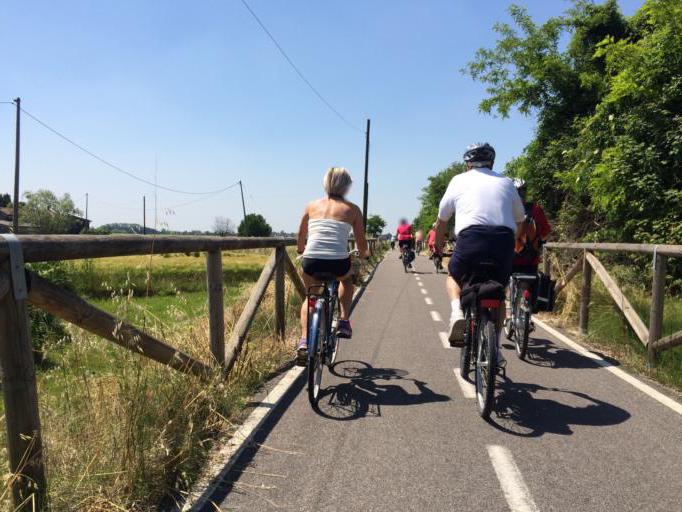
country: IT
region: Veneto
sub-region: Provincia di Vicenza
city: Ponte di Barbarano
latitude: 45.4071
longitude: 11.5785
